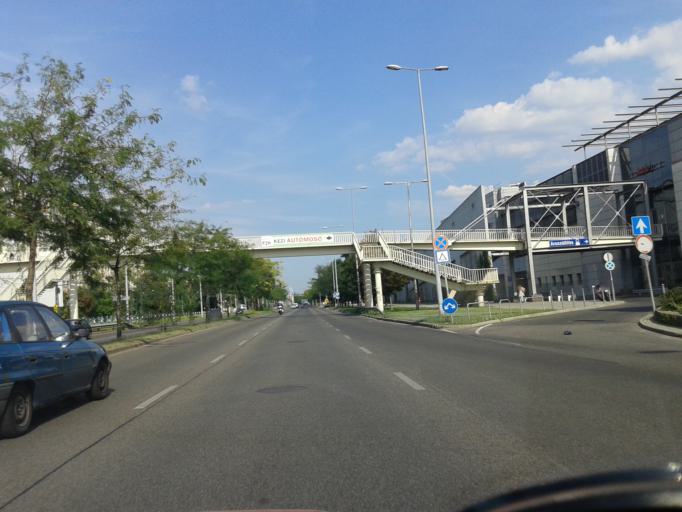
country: HU
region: Budapest
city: Budapest X. keruelet
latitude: 47.5033
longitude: 19.1379
